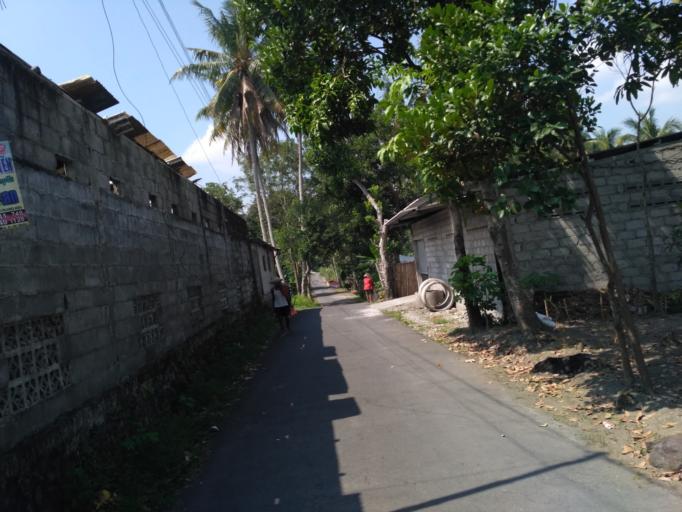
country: ID
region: Daerah Istimewa Yogyakarta
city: Melati
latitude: -7.7046
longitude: 110.4130
